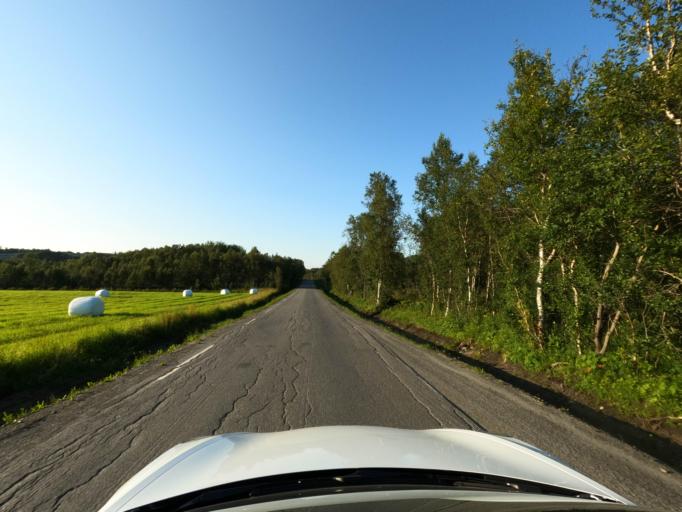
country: NO
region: Troms
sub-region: Skanland
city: Evenskjer
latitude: 68.4705
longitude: 16.7034
